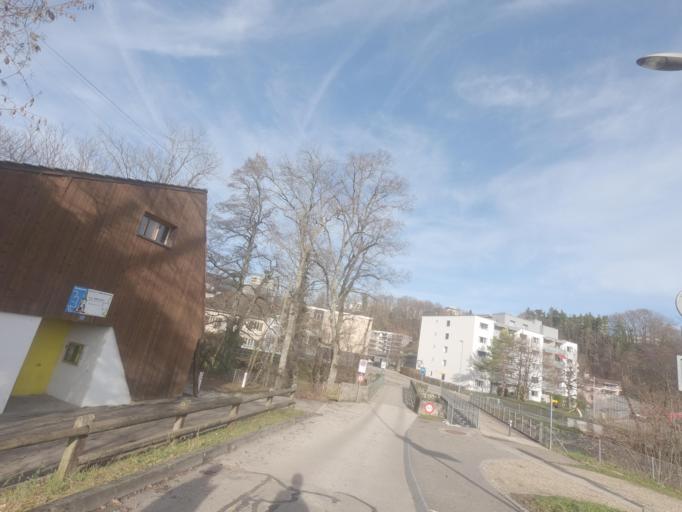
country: CH
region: Neuchatel
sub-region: Boudry District
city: Boudry
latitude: 46.9526
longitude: 6.8331
